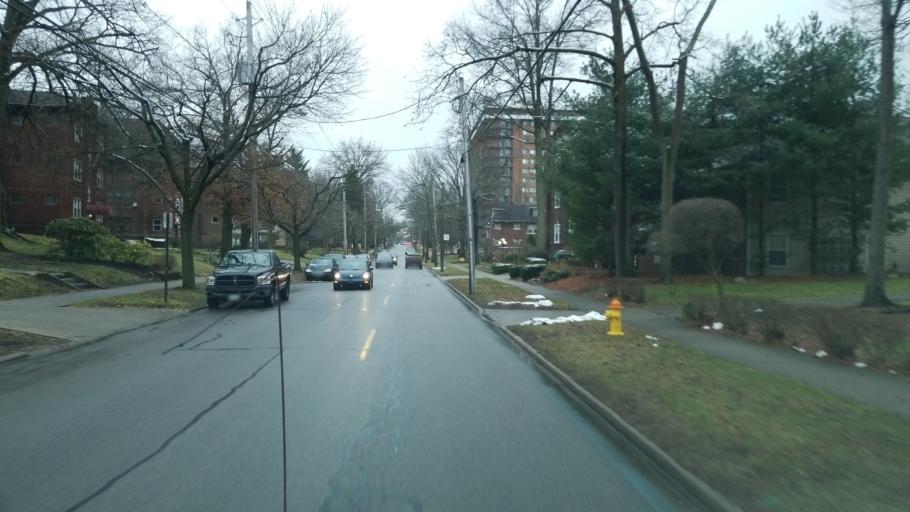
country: US
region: Ohio
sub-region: Summit County
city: Akron
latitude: 41.1012
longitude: -81.5465
